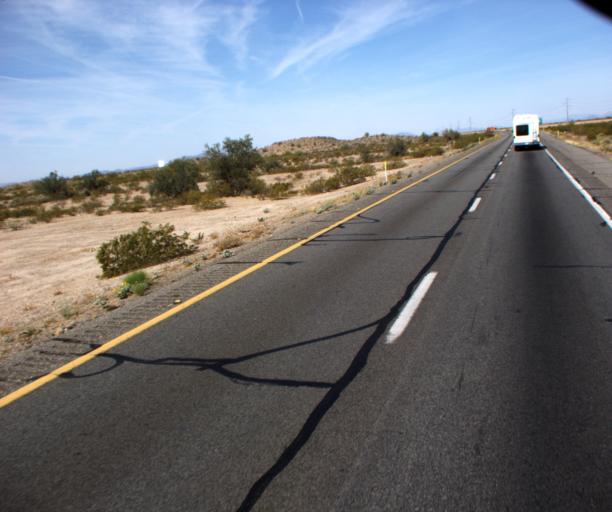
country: US
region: Arizona
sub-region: Maricopa County
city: Buckeye
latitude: 33.4314
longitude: -112.6390
